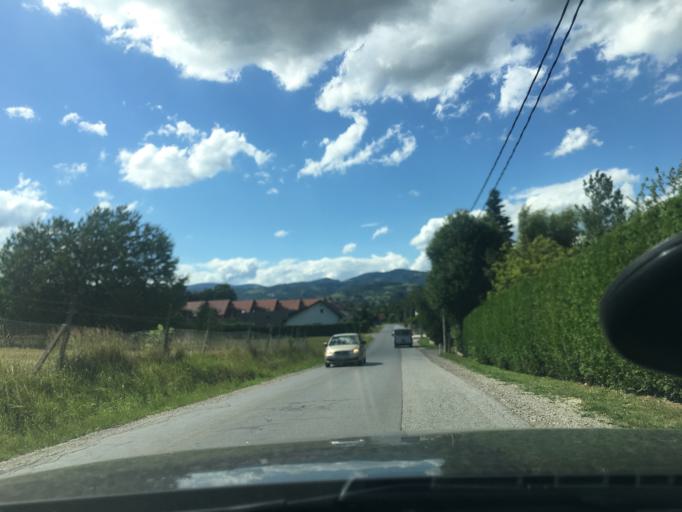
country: SI
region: Maribor
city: Pekre
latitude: 46.5454
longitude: 15.6003
